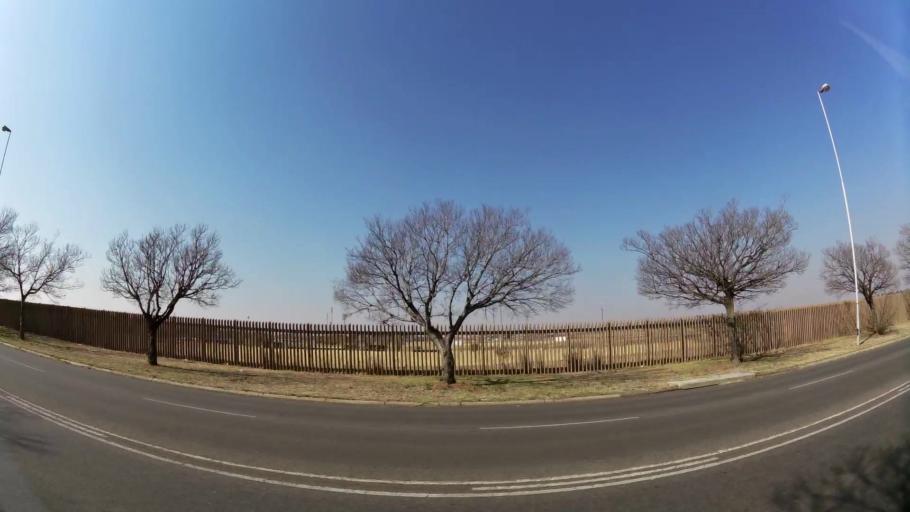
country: ZA
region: Gauteng
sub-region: Ekurhuleni Metropolitan Municipality
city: Boksburg
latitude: -26.2324
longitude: 28.2705
